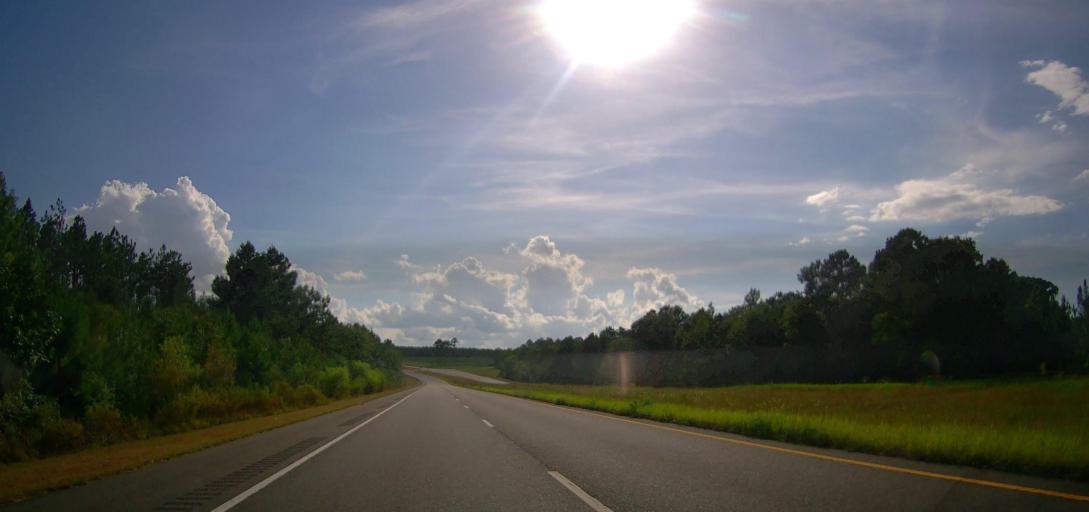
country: US
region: Georgia
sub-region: Talbot County
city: Talbotton
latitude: 32.5835
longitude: -84.5160
